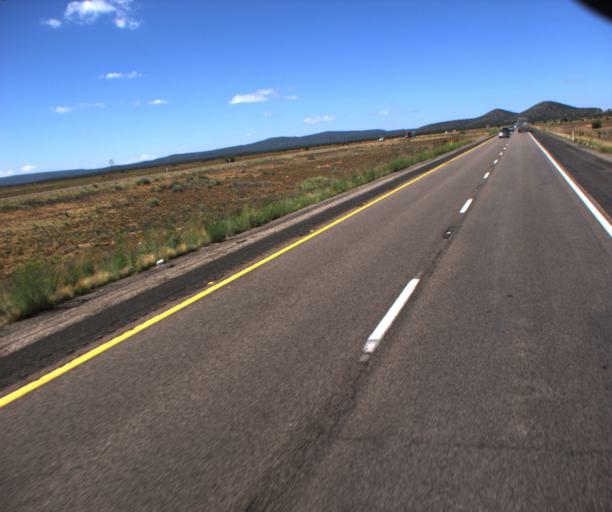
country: US
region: Arizona
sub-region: Mohave County
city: Peach Springs
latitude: 35.3101
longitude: -112.9807
